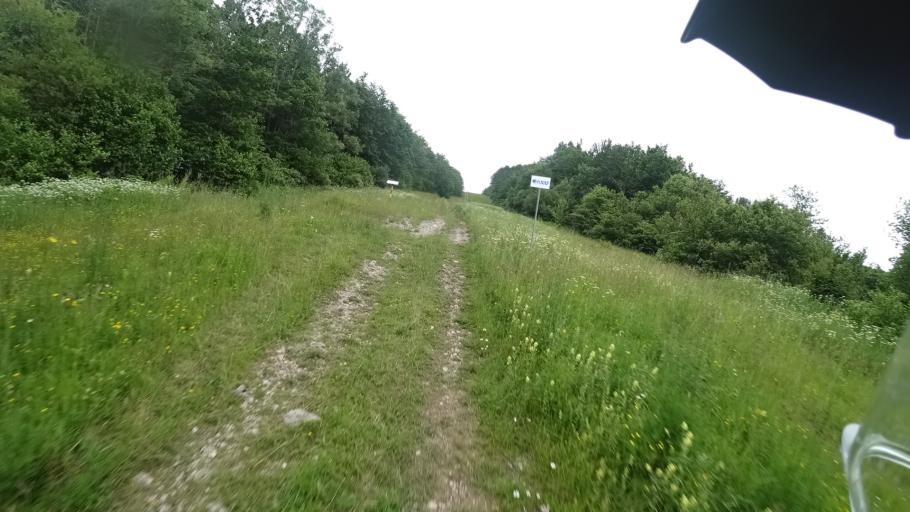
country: HR
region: Primorsko-Goranska
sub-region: Grad Delnice
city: Delnice
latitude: 45.3825
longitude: 14.8563
